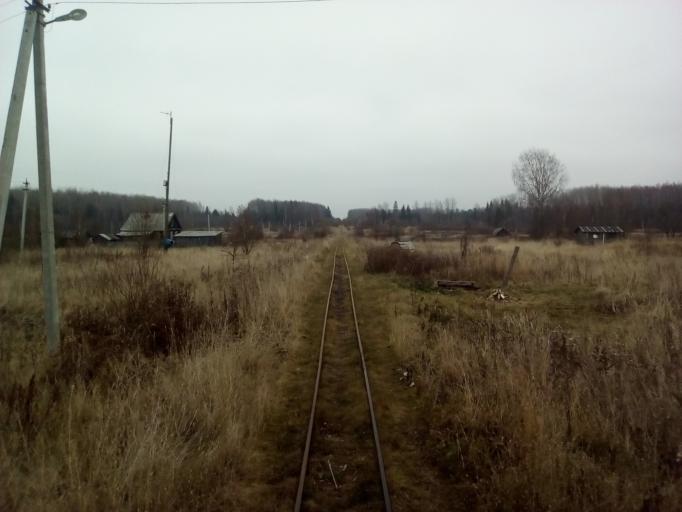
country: RU
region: Vologda
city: Kharovsk
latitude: 59.8029
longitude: 40.4608
